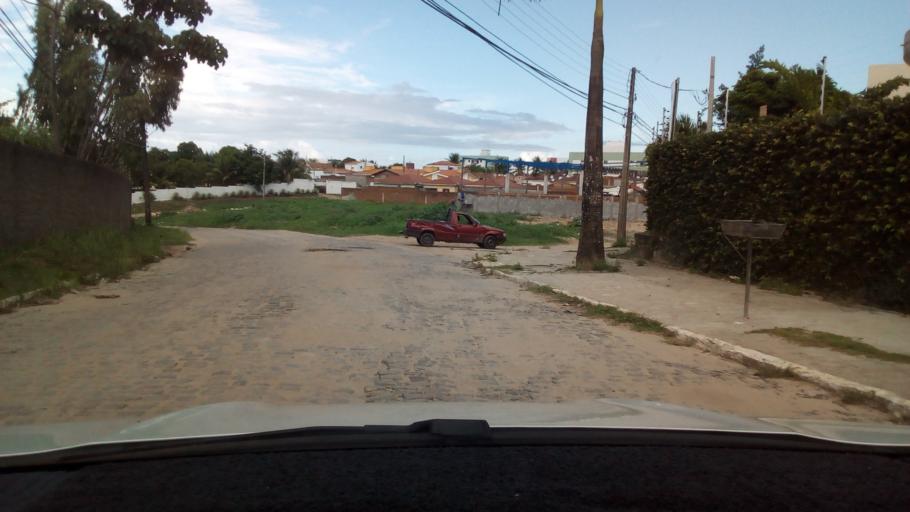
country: BR
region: Paraiba
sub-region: Joao Pessoa
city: Joao Pessoa
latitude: -7.1630
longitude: -34.8527
